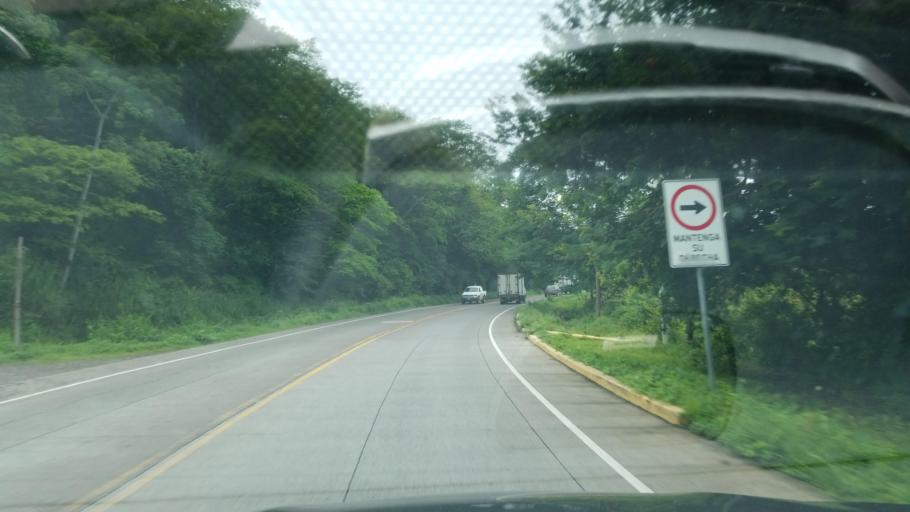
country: HN
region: Francisco Morazan
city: El Porvenir
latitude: 13.6823
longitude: -87.3562
